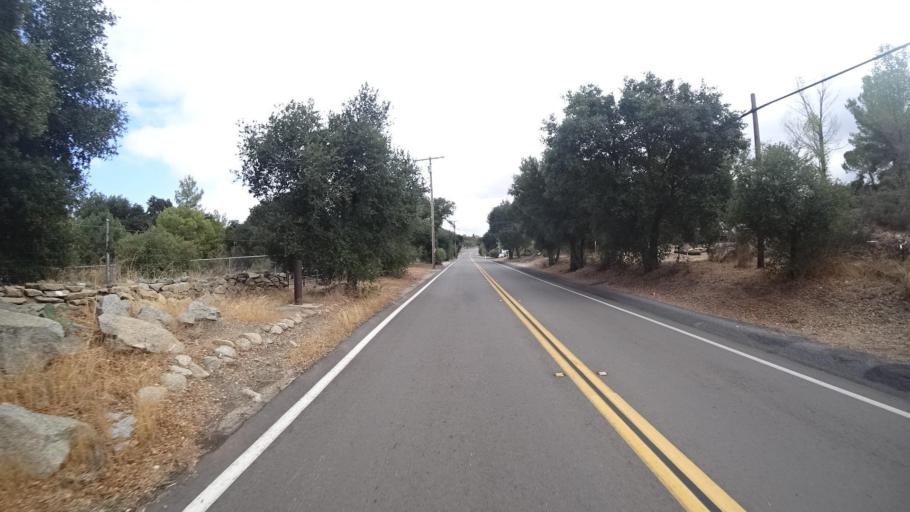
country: US
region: California
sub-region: San Diego County
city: Campo
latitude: 32.6775
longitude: -116.5084
